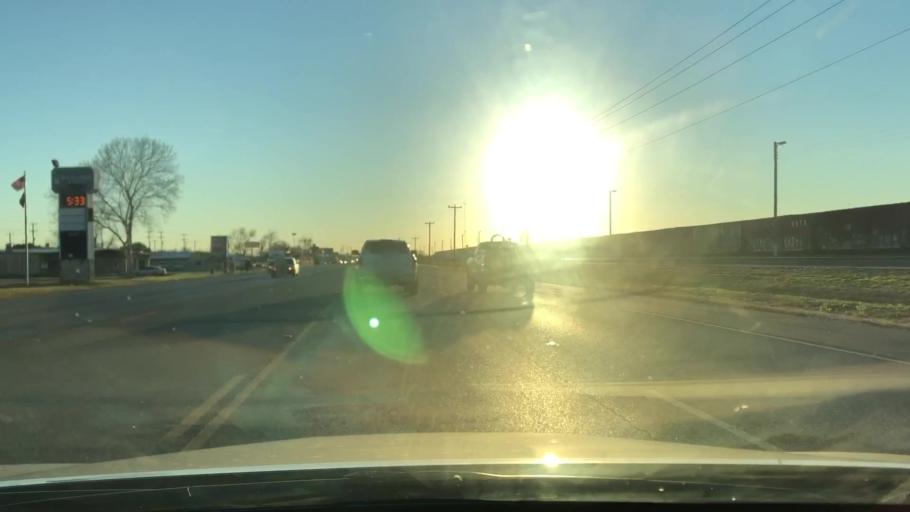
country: US
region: Texas
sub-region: Bexar County
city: Kirby
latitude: 29.4669
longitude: -98.3927
